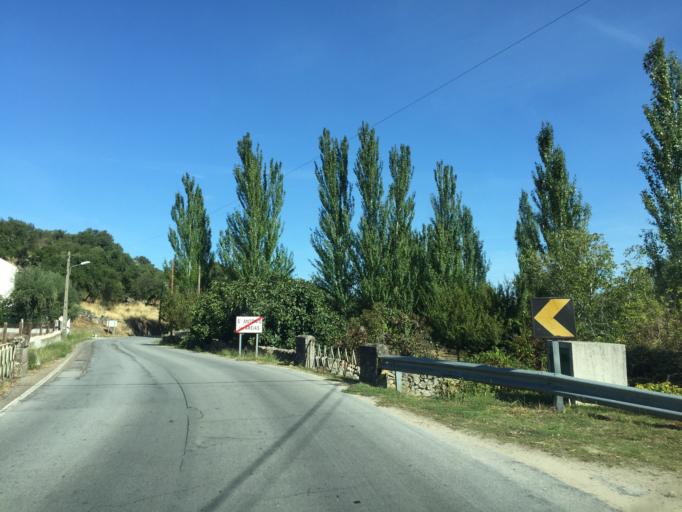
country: PT
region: Portalegre
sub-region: Marvao
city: Marvao
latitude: 39.4178
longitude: -7.3520
